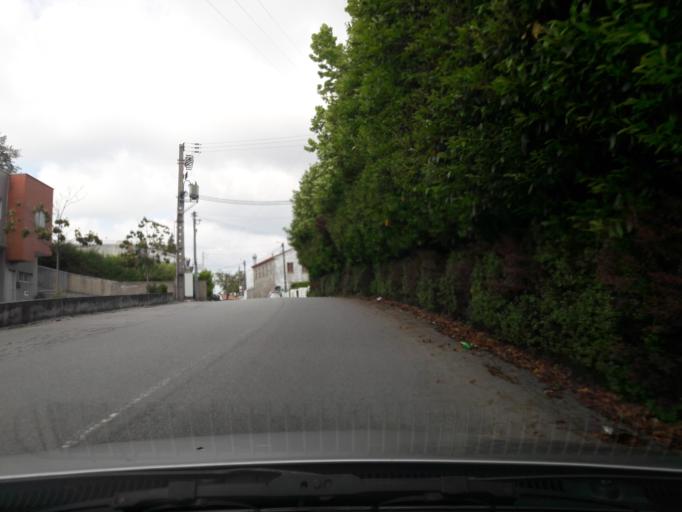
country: PT
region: Braga
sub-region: Guimaraes
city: Candoso
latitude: 41.4195
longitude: -8.3207
